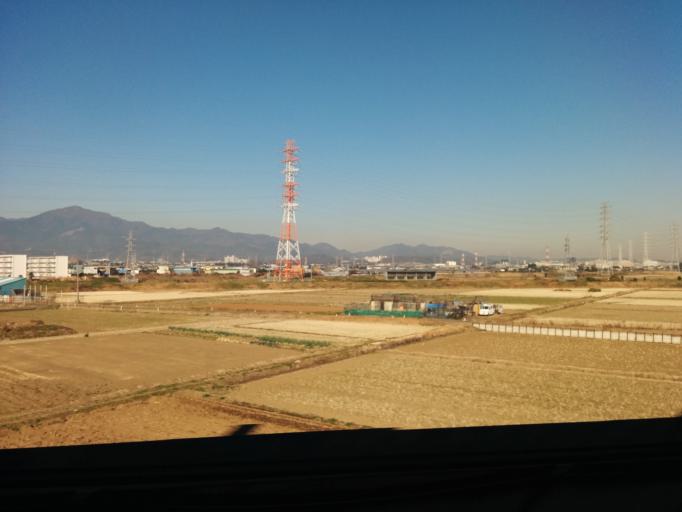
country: JP
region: Kanagawa
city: Isehara
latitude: 35.3770
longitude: 139.3500
